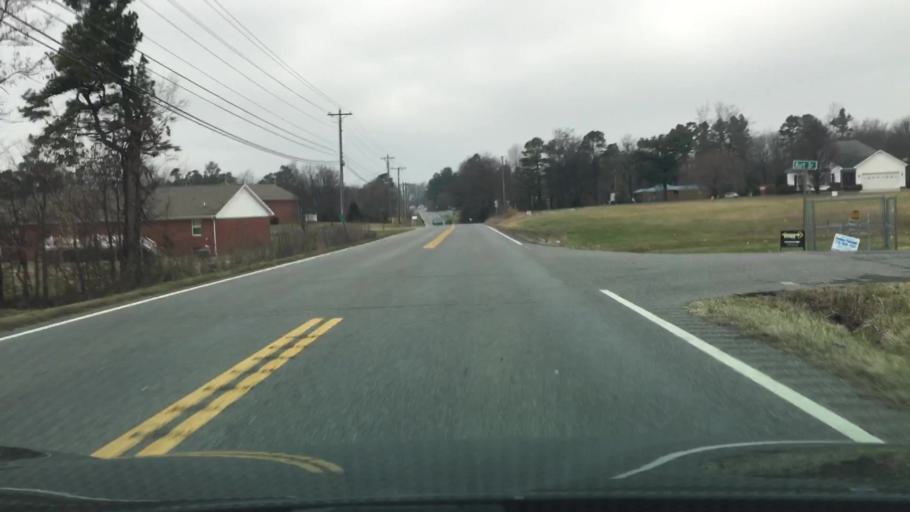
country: US
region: Kentucky
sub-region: Marshall County
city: Benton
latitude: 36.9438
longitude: -88.3633
